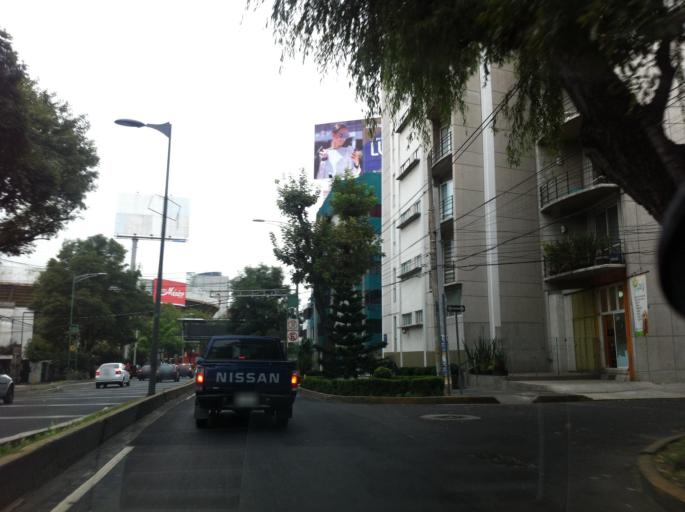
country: MX
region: Mexico City
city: Colonia del Valle
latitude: 19.3833
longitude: -99.1823
